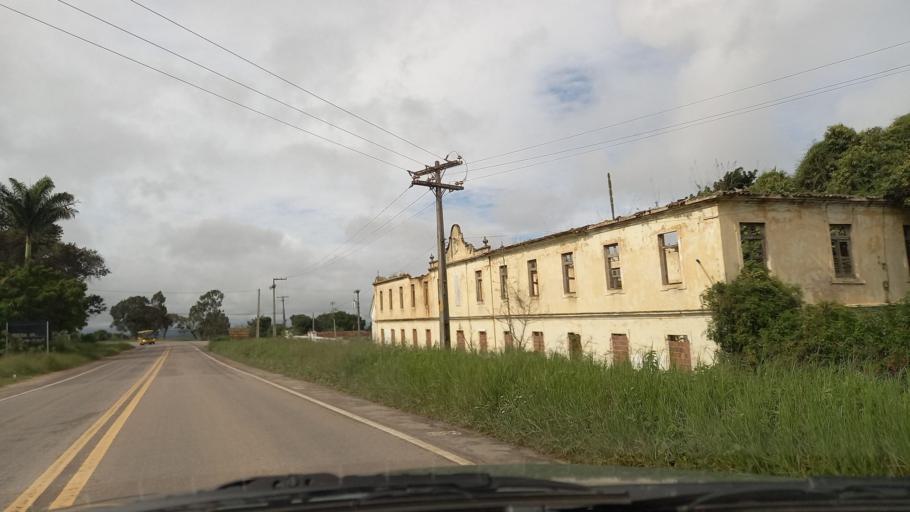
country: BR
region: Pernambuco
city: Garanhuns
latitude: -8.9094
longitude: -36.4962
